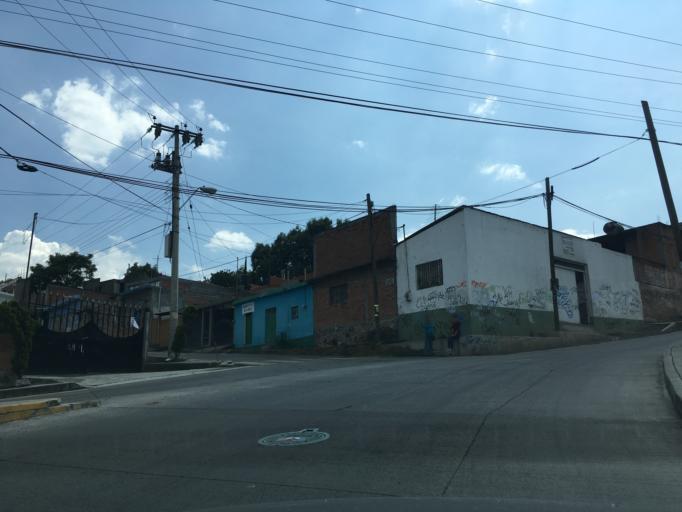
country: MX
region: Michoacan
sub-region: Morelia
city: Montana Monarca (Punta Altozano)
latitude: 19.6679
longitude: -101.1841
